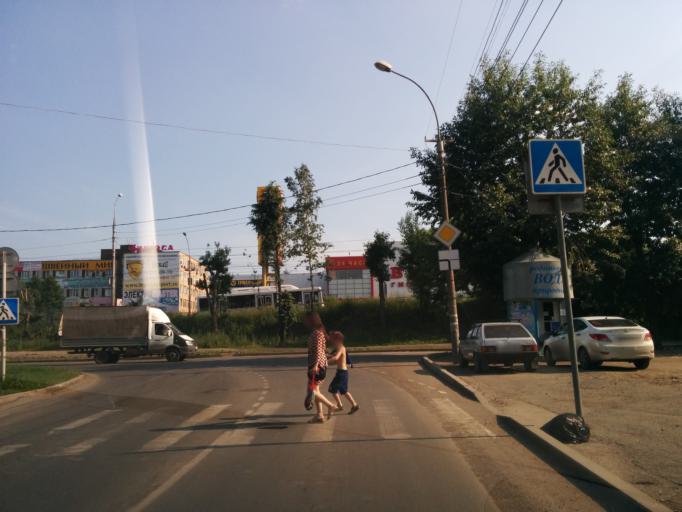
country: RU
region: Perm
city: Perm
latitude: 57.9945
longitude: 56.2092
